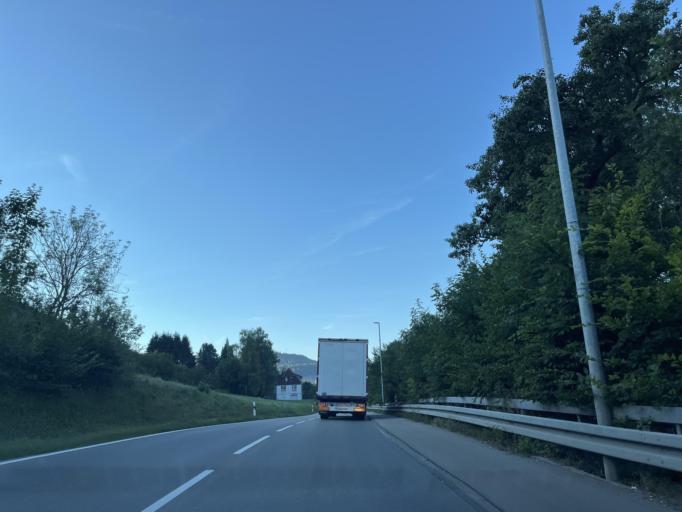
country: DE
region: Baden-Wuerttemberg
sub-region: Tuebingen Region
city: Jungingen
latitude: 48.3109
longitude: 9.0628
